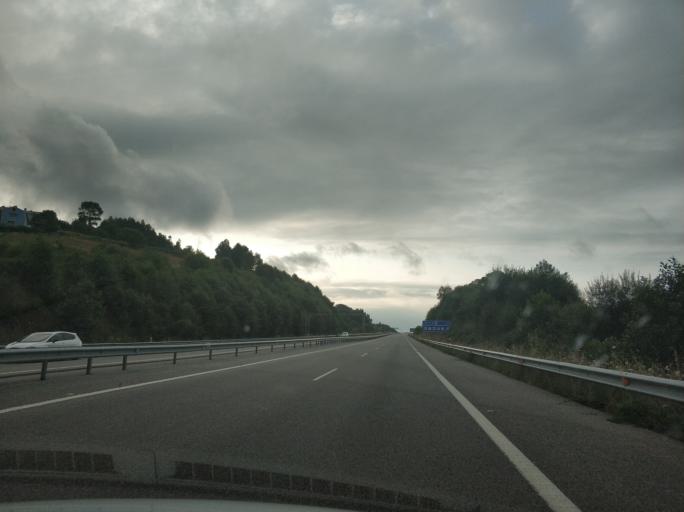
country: ES
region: Asturias
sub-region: Province of Asturias
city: Cudillero
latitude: 43.5465
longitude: -6.1600
